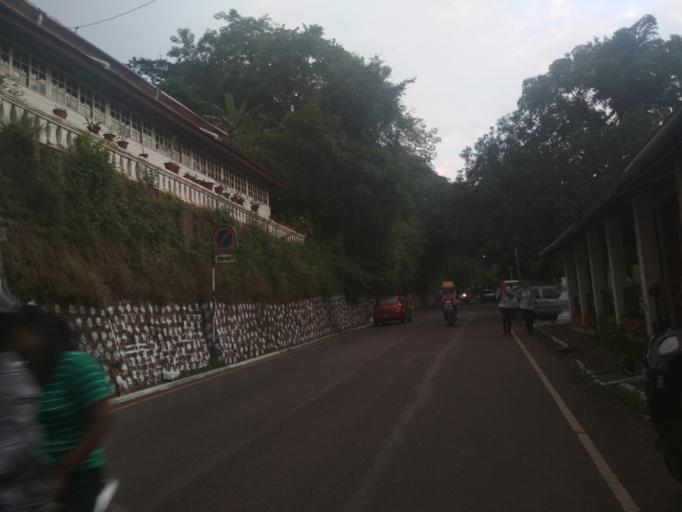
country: IN
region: Goa
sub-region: North Goa
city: Panaji
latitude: 15.4960
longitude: 73.8279
